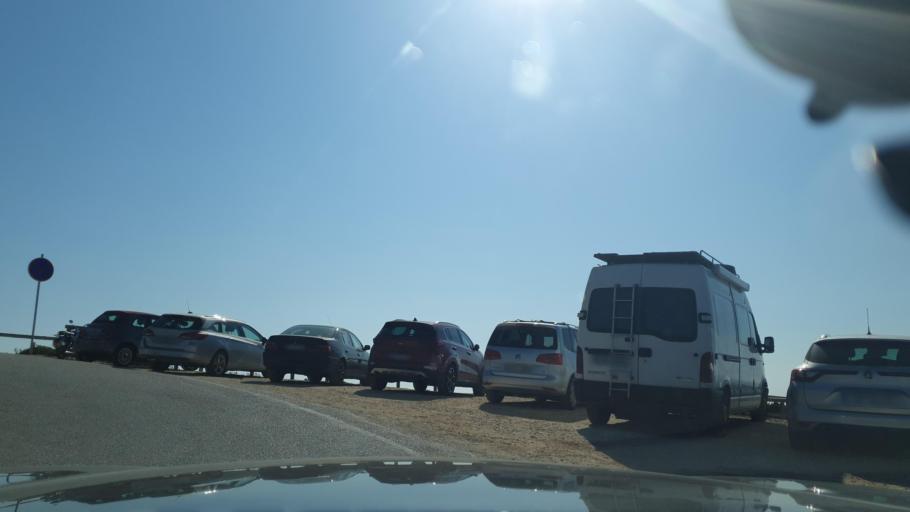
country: PT
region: Beja
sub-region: Odemira
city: Sao Teotonio
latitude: 37.4390
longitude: -8.7994
